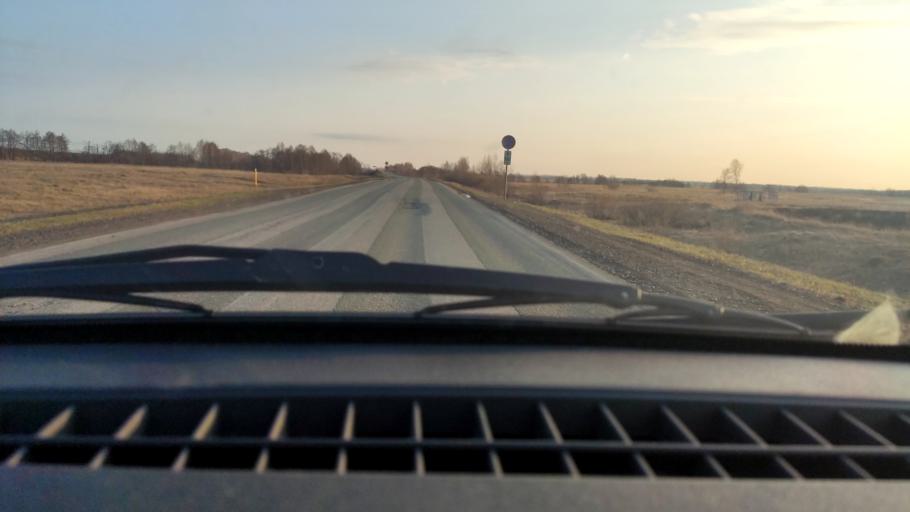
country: RU
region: Bashkortostan
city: Chishmy
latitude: 54.4452
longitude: 55.2430
